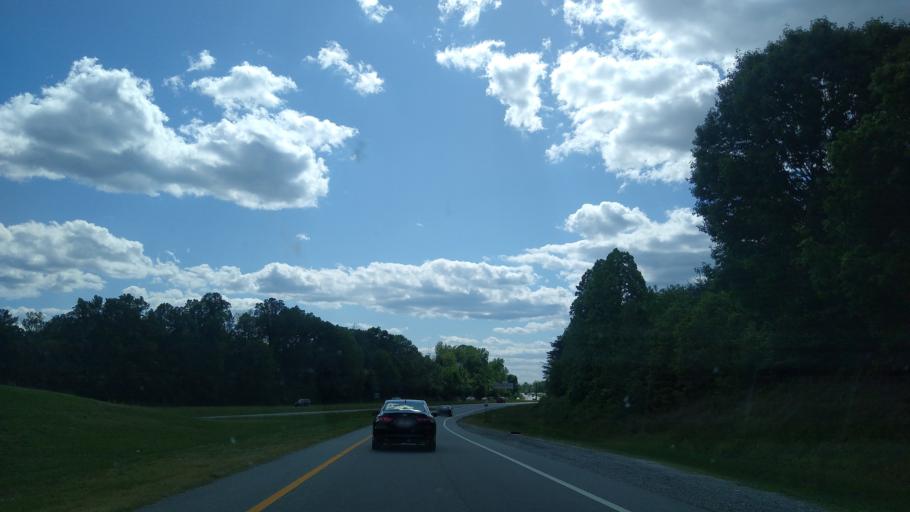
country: US
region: North Carolina
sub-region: Guilford County
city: High Point
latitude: 36.0102
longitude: -80.0113
